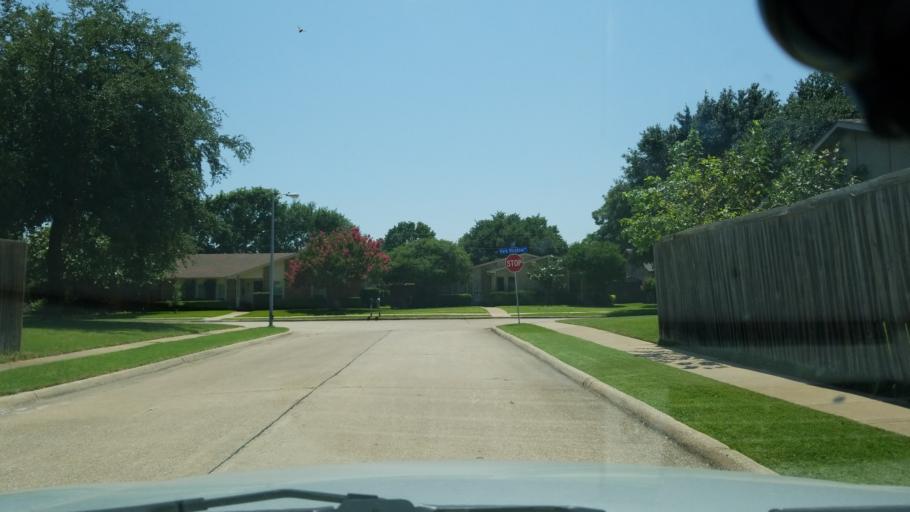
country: US
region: Texas
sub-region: Dallas County
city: Coppell
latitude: 32.9621
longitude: -96.9867
